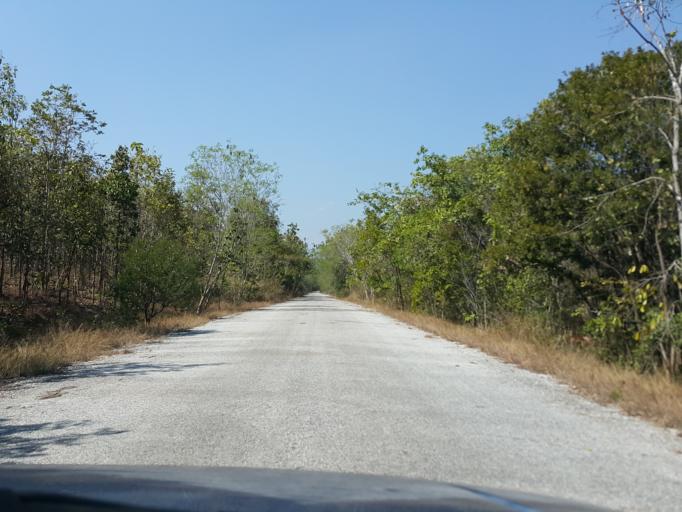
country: TH
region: Chiang Mai
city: Doi Lo
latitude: 18.5319
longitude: 98.7445
